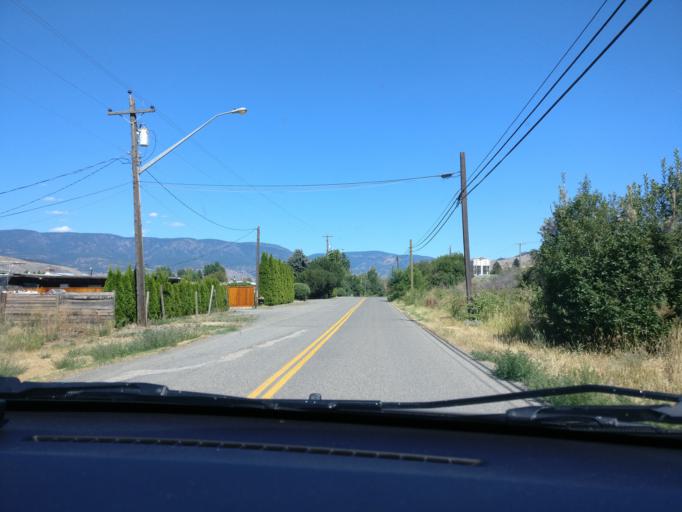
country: CA
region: British Columbia
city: Logan Lake
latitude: 50.7558
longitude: -120.8294
